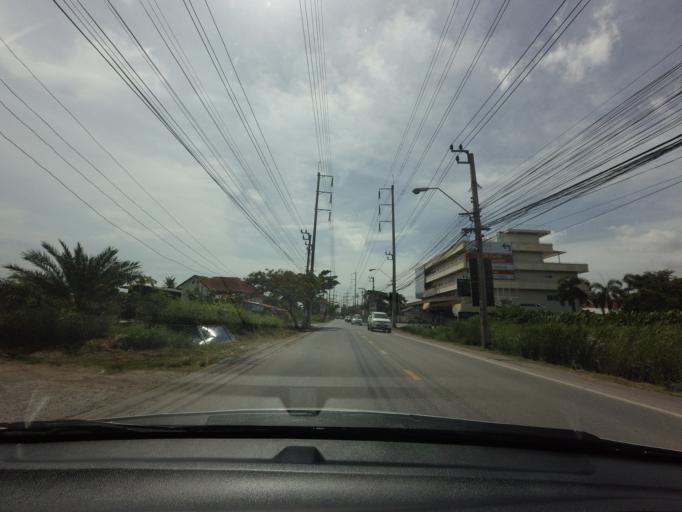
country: TH
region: Bangkok
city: Bang Na
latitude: 13.6174
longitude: 100.6702
